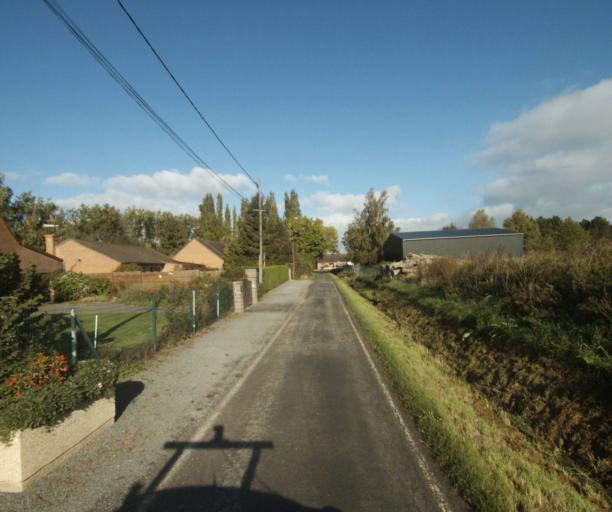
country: FR
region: Nord-Pas-de-Calais
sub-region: Departement du Nord
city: Perenchies
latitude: 50.6838
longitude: 2.9672
